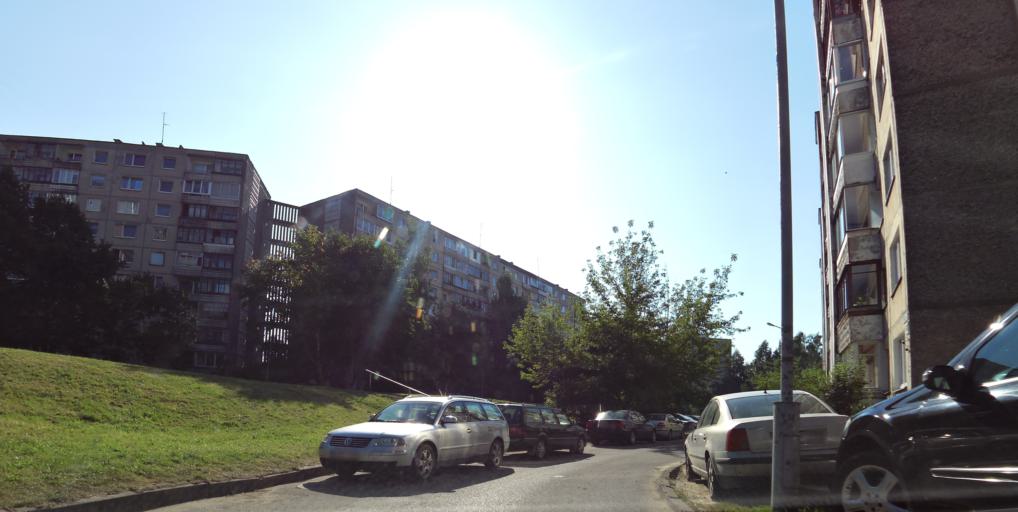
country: LT
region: Vilnius County
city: Justiniskes
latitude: 54.7068
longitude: 25.2218
